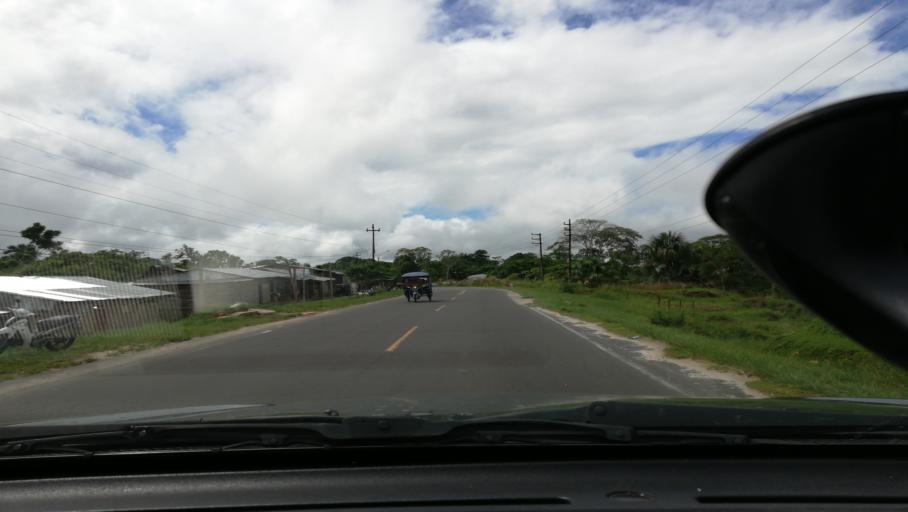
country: PE
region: Loreto
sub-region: Provincia de Maynas
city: Iquitos
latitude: -3.8655
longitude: -73.3396
